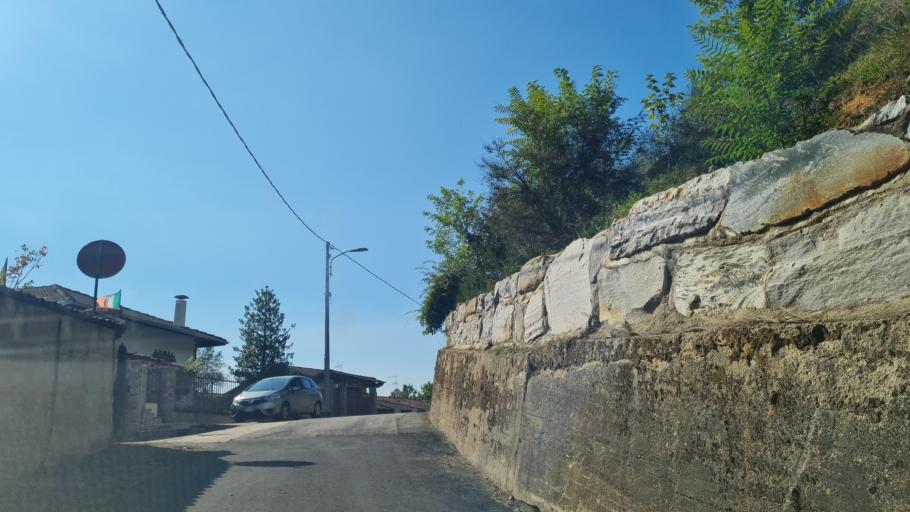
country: IT
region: Piedmont
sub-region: Provincia di Biella
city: Quaregna
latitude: 45.5872
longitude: 8.1636
